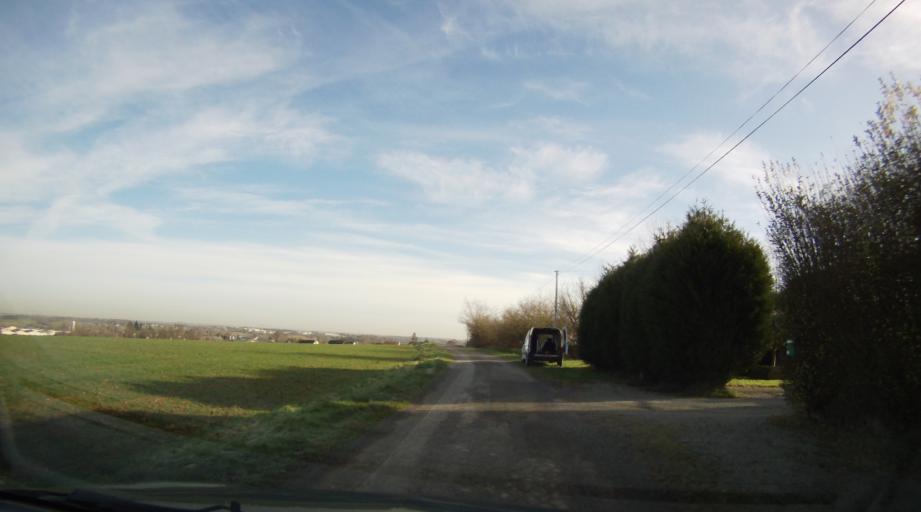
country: FR
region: Brittany
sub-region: Departement d'Ille-et-Vilaine
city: Bourgbarre
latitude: 47.9862
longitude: -1.6217
